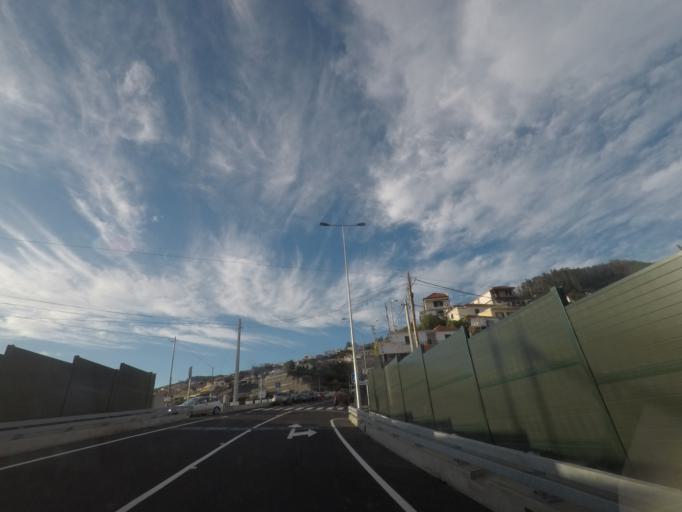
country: PT
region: Madeira
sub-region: Funchal
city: Nossa Senhora do Monte
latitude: 32.6772
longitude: -16.9400
